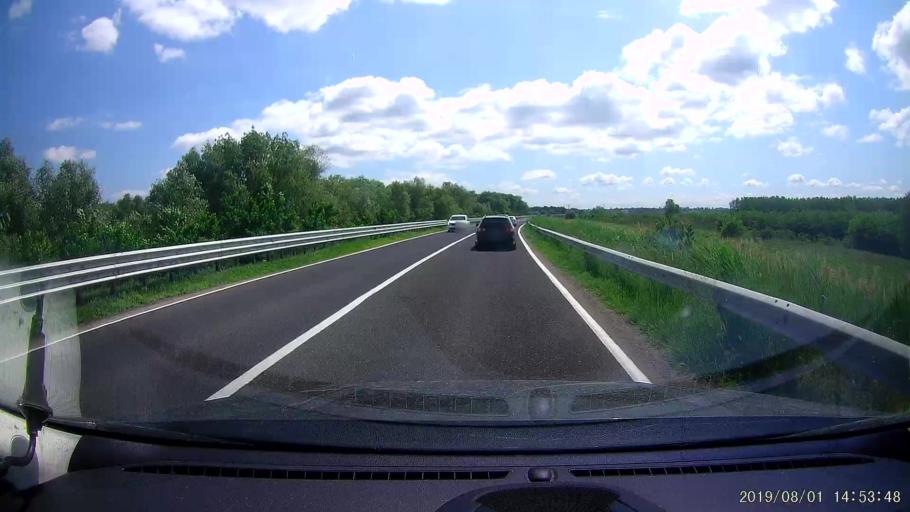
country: RO
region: Braila
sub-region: Municipiul Braila
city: Braila
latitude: 45.3285
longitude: 27.9984
